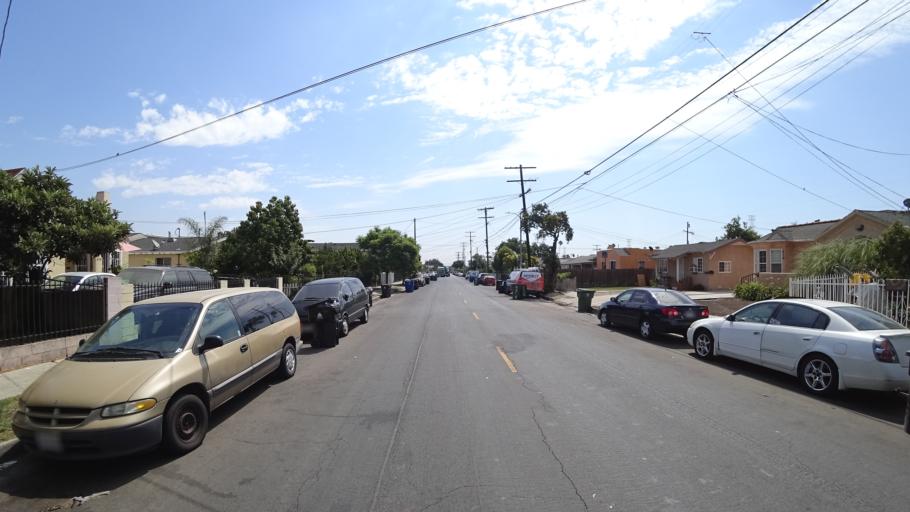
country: US
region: California
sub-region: Los Angeles County
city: Westmont
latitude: 33.9491
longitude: -118.2855
